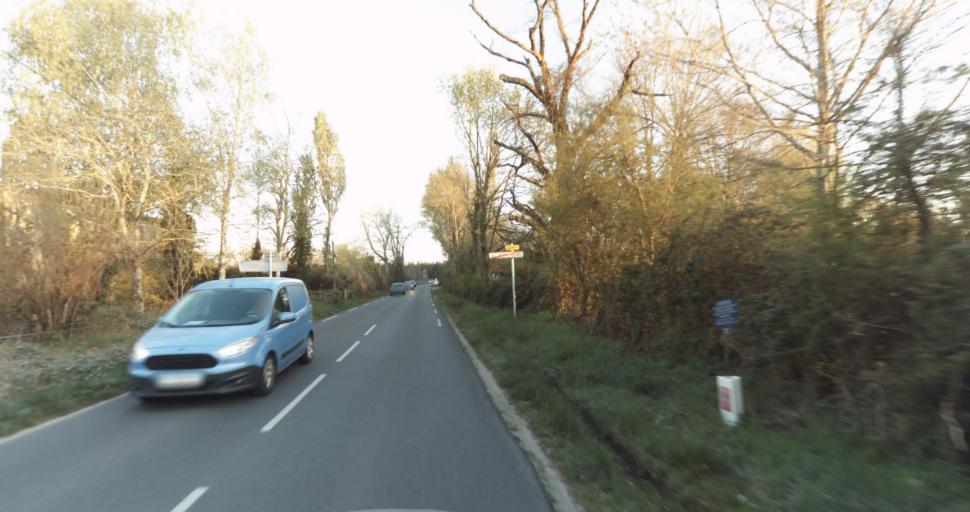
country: FR
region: Aquitaine
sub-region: Departement de la Gironde
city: Martignas-sur-Jalle
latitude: 44.8159
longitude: -0.7494
